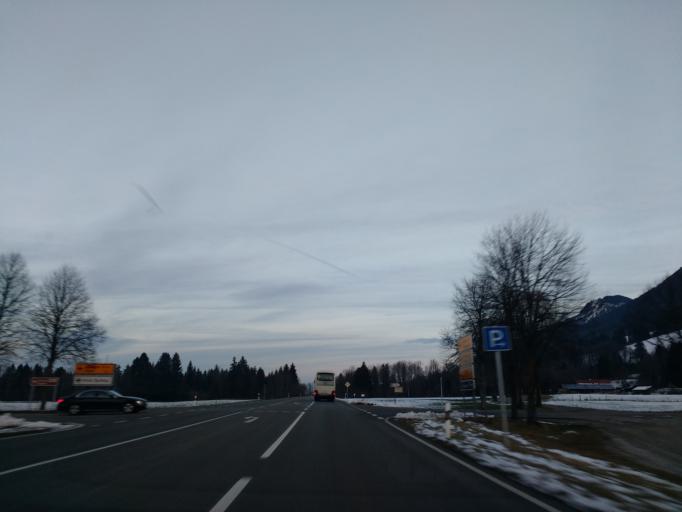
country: DE
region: Bavaria
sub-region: Swabia
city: Halblech
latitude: 47.6241
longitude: 10.8146
